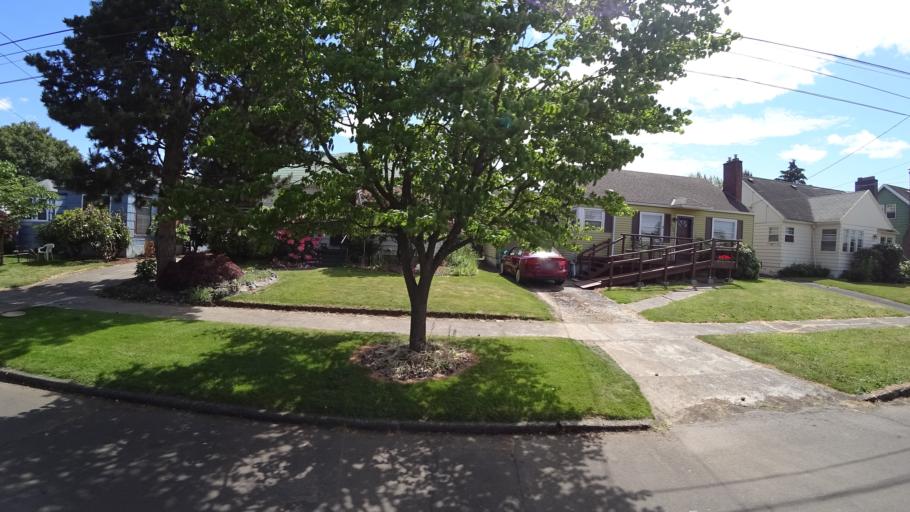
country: US
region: Oregon
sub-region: Washington County
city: West Haven
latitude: 45.5841
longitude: -122.7309
